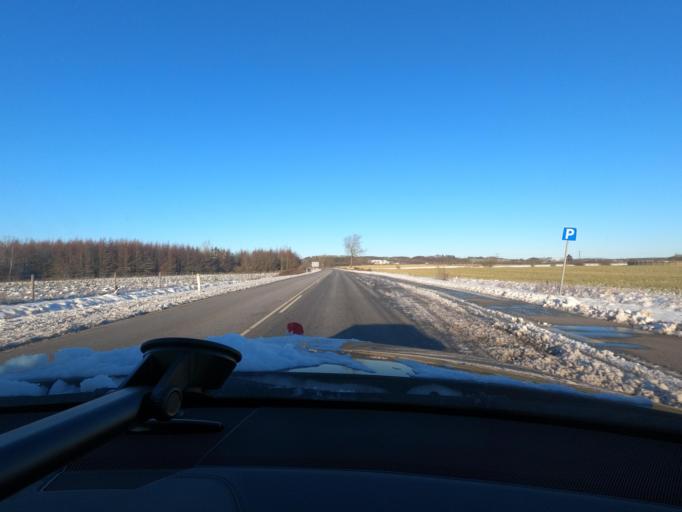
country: DK
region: South Denmark
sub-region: Aabenraa Kommune
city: Rodekro
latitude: 55.0773
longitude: 9.2204
